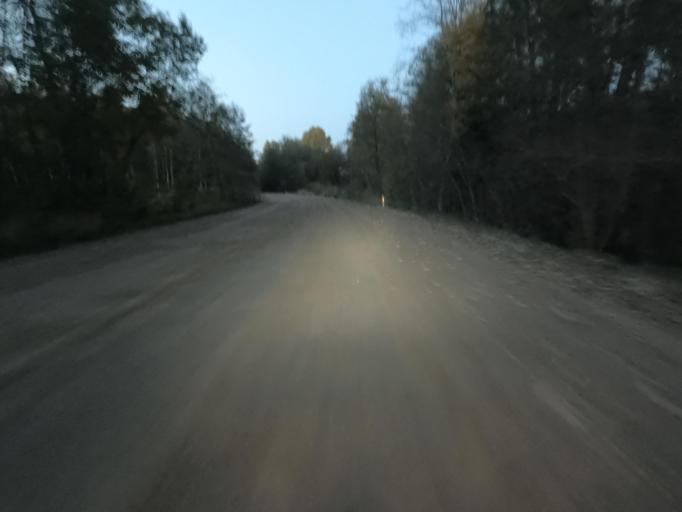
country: RU
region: Leningrad
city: Lyuban'
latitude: 59.1885
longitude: 31.2504
